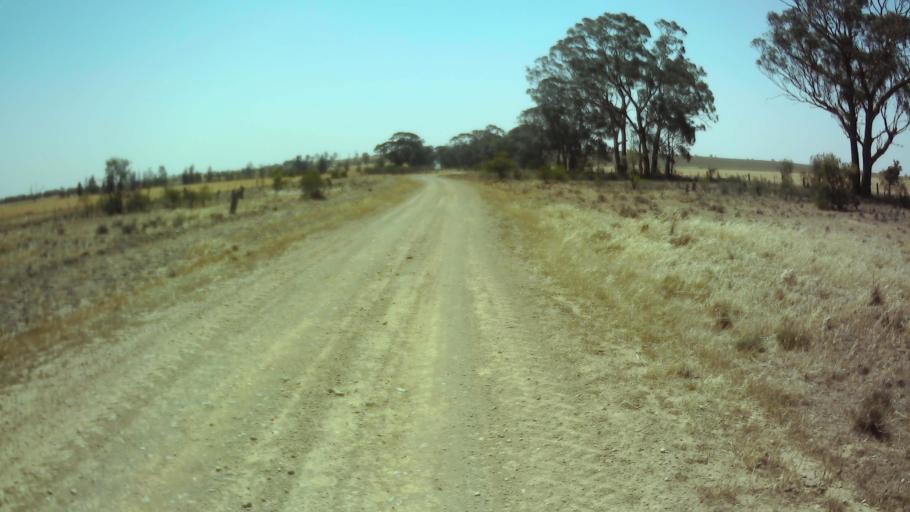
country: AU
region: New South Wales
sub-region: Weddin
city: Grenfell
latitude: -33.9130
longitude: 147.7701
